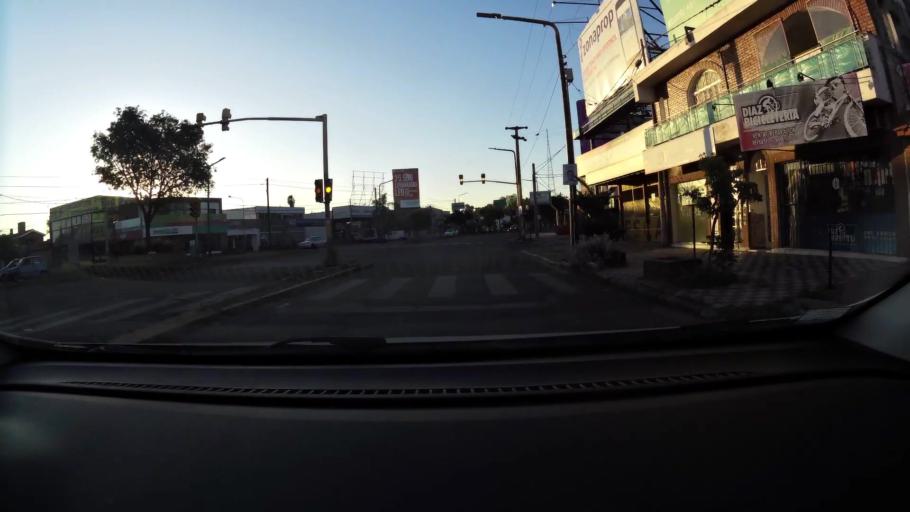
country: AR
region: Cordoba
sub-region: Departamento de Capital
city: Cordoba
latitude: -31.3858
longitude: -64.2189
